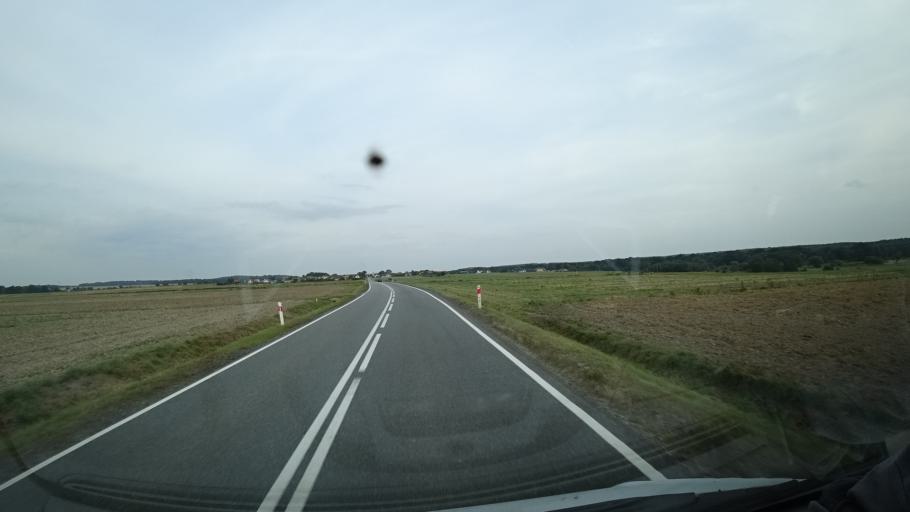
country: PL
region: Silesian Voivodeship
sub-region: Powiat gliwicki
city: Rudziniec
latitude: 50.3861
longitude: 18.4142
